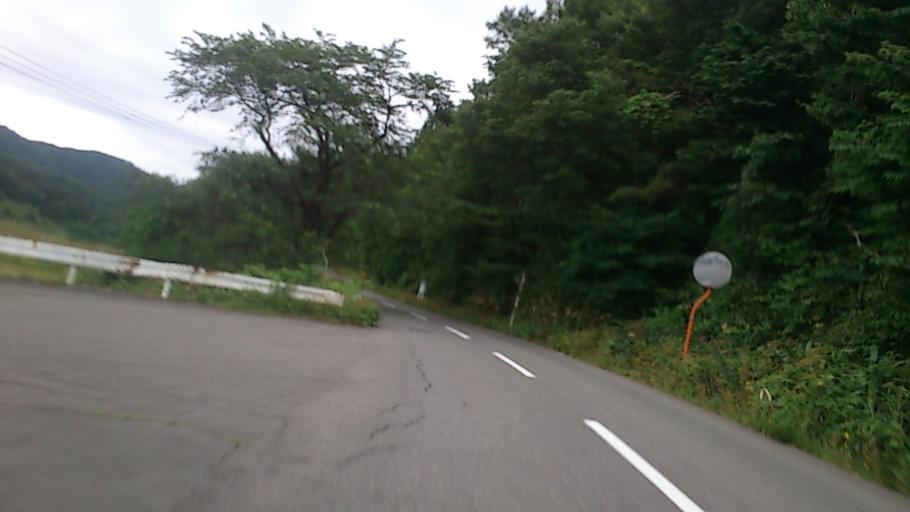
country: JP
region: Yamagata
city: Tsuruoka
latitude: 38.7384
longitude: 139.9602
